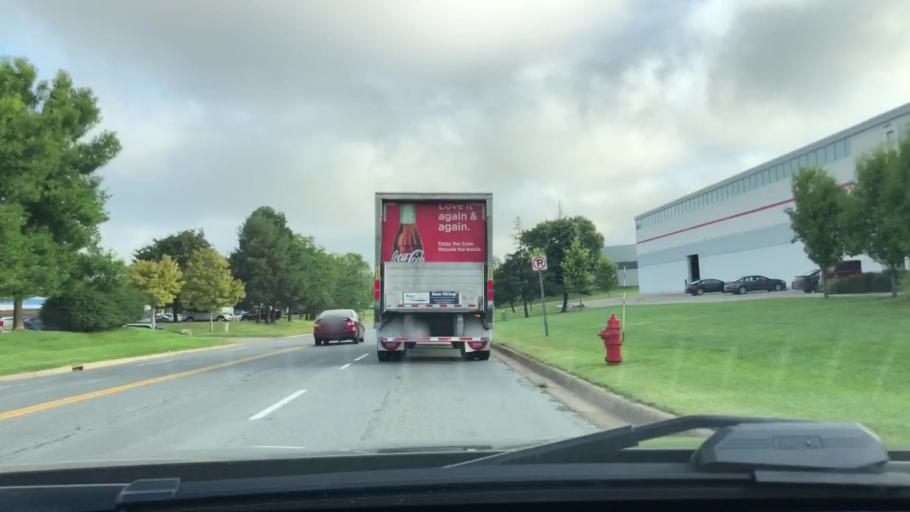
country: US
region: Minnesota
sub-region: Dakota County
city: Mendota Heights
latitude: 44.8499
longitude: -93.1589
